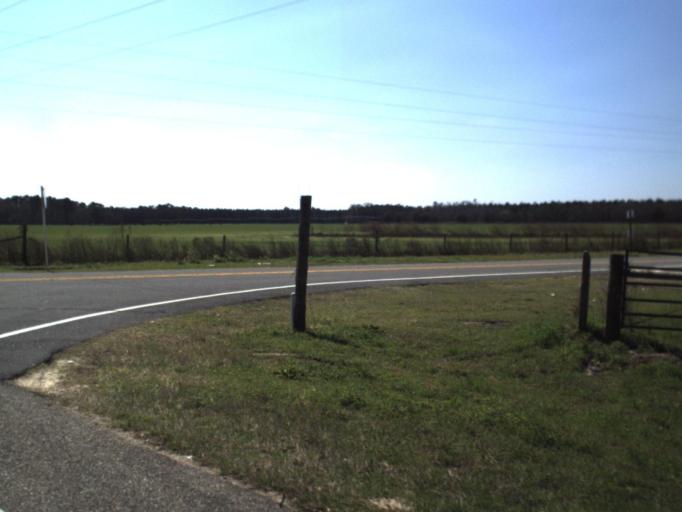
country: US
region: Florida
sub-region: Calhoun County
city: Blountstown
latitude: 30.5763
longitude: -85.0219
